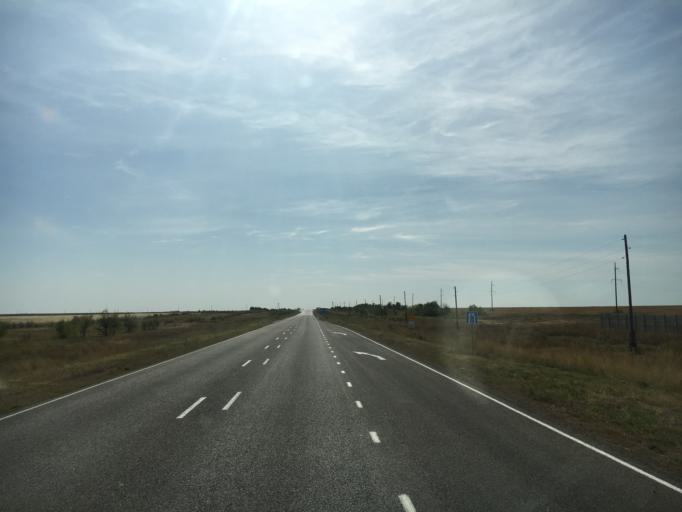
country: KZ
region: Batys Qazaqstan
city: Peremetnoe
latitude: 51.1323
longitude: 50.8990
